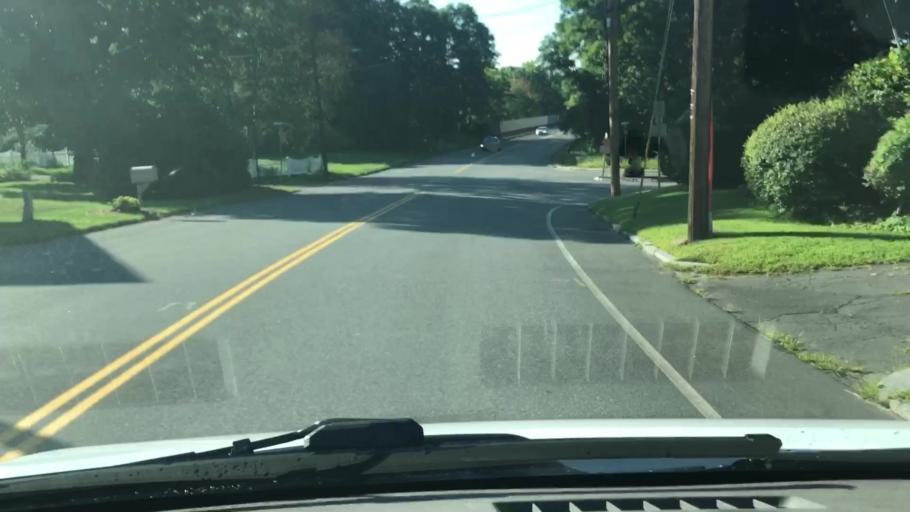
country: US
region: Massachusetts
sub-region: Franklin County
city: Greenfield
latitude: 42.6085
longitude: -72.6127
